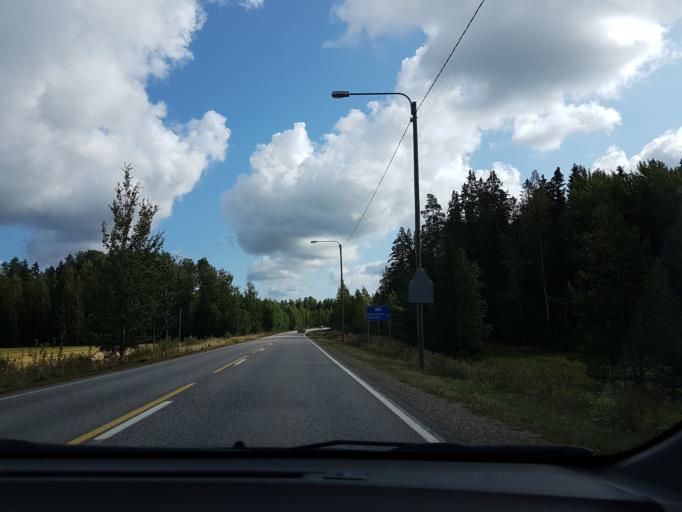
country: FI
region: Uusimaa
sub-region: Helsinki
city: Sibbo
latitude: 60.4738
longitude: 25.2123
